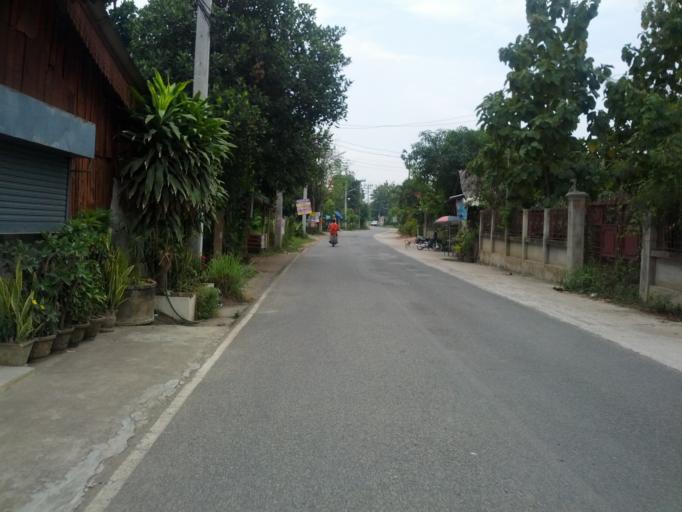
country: TH
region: Chiang Mai
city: San Kamphaeng
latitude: 18.7675
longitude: 99.1129
